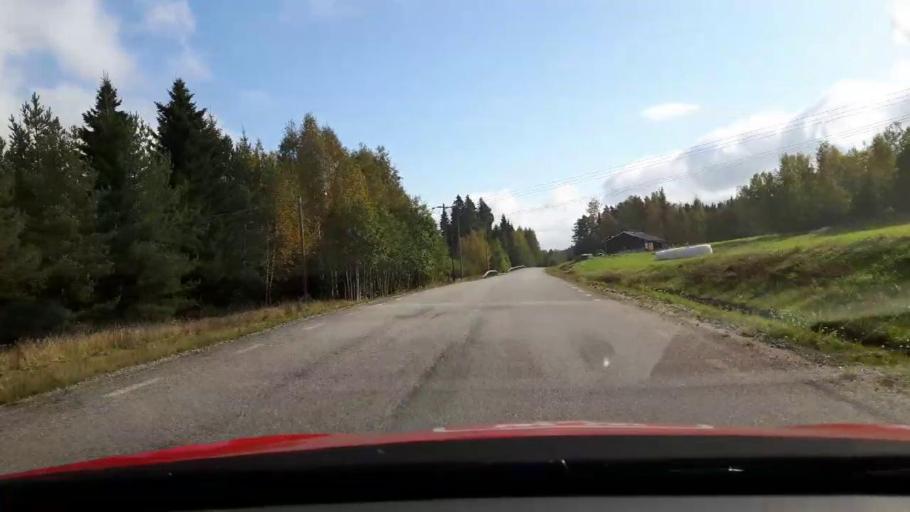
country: SE
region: Gaevleborg
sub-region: Ljusdals Kommun
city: Ljusdal
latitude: 61.7688
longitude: 16.0197
